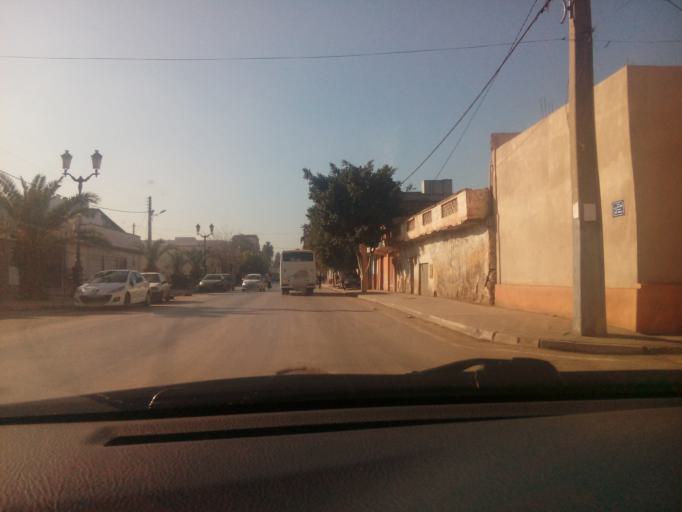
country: DZ
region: Oran
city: Es Senia
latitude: 35.6486
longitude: -0.6161
